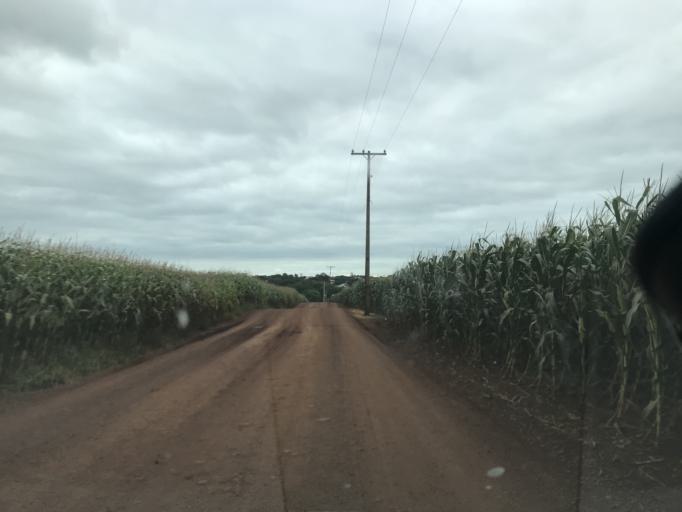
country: BR
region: Parana
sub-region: Palotina
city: Palotina
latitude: -24.3061
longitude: -53.8248
